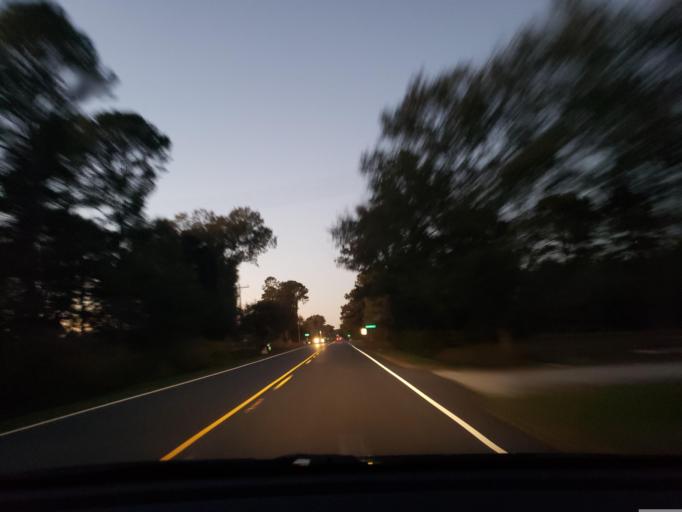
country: US
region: North Carolina
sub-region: Duplin County
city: Kenansville
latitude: 34.9263
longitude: -77.9381
